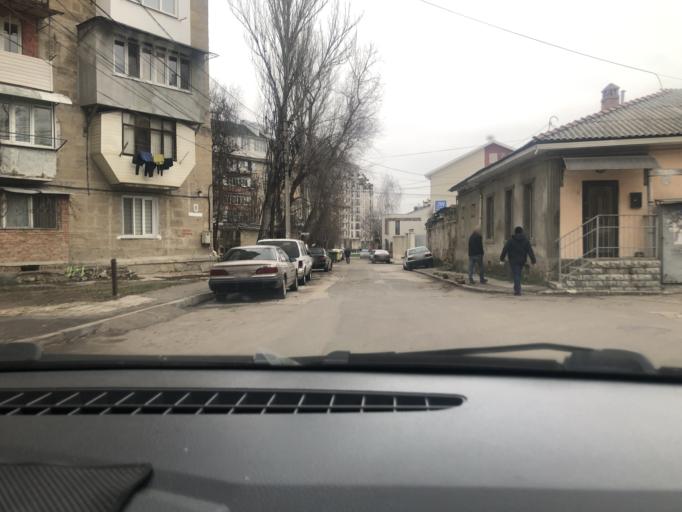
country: MD
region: Chisinau
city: Chisinau
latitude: 47.0284
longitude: 28.8431
